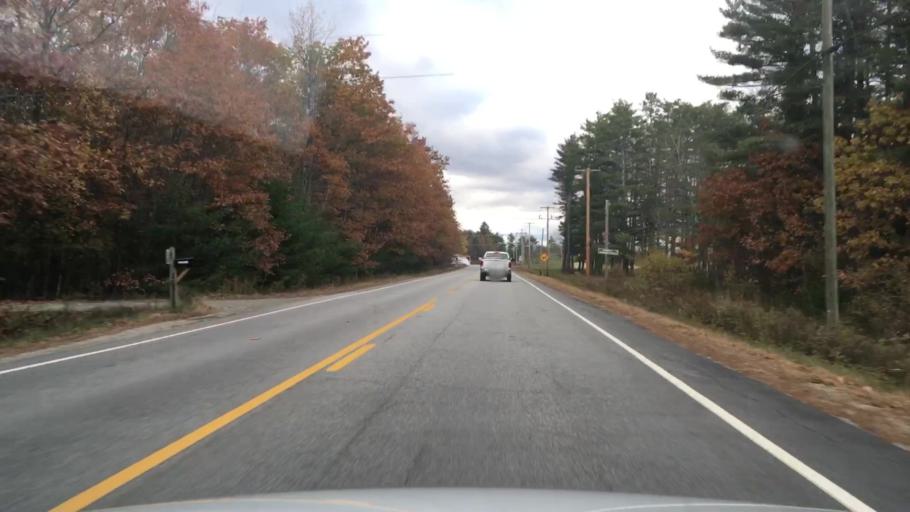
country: US
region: Maine
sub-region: Androscoggin County
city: Leeds
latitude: 44.3402
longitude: -70.1321
